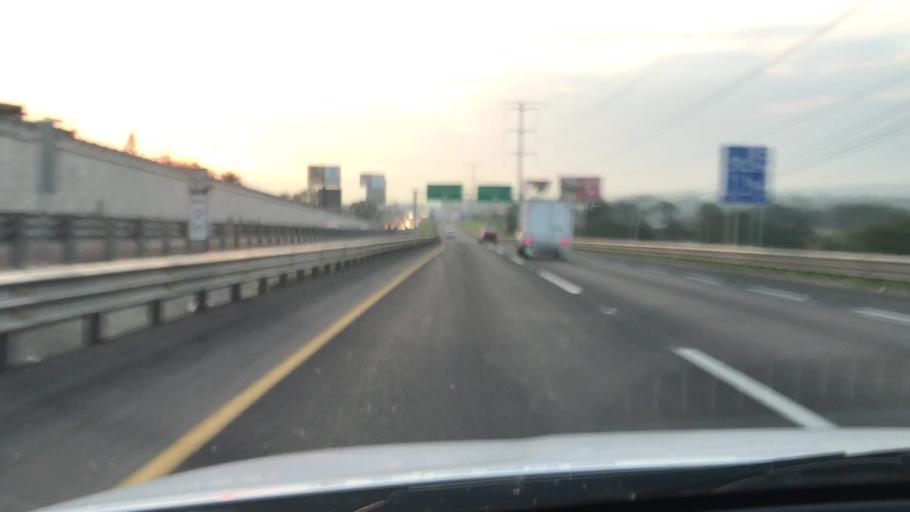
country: MX
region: Jalisco
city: Tonala
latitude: 20.6166
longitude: -103.2379
